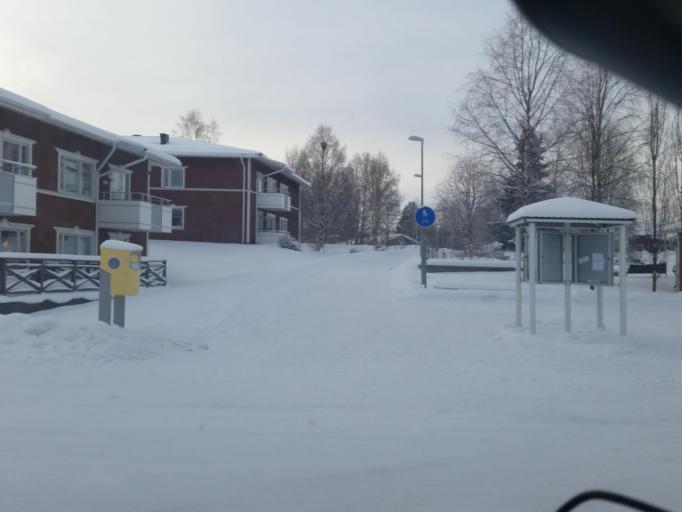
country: SE
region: Norrbotten
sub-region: Pitea Kommun
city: Rosvik
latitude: 65.4309
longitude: 21.6910
